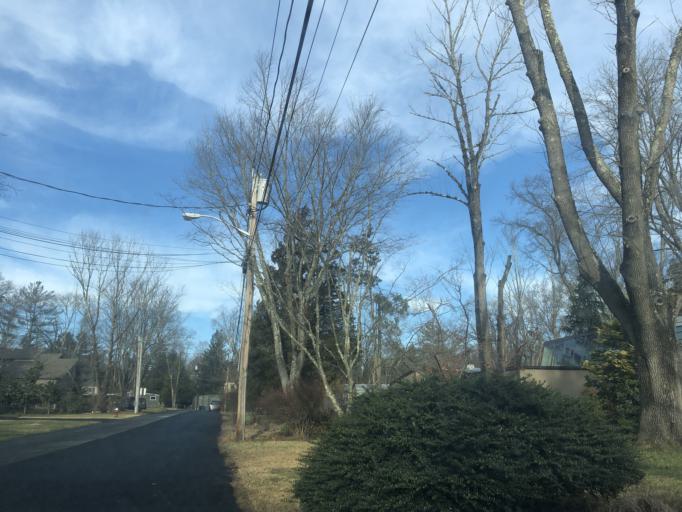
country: US
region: New Jersey
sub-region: Mercer County
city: Princeton
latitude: 40.3618
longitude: -74.6405
